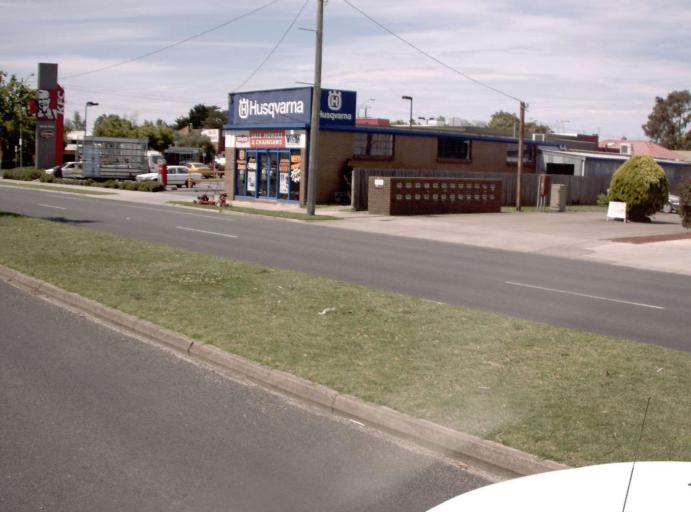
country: AU
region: Victoria
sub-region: Wellington
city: Sale
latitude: -38.1060
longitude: 147.0681
